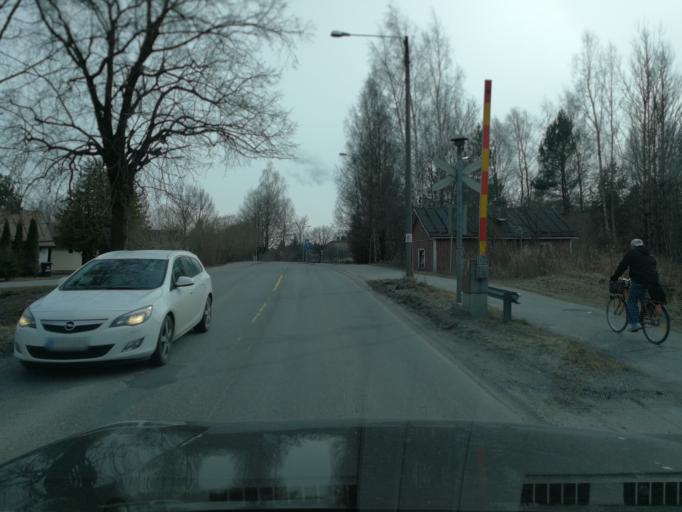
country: FI
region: Uusimaa
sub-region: Helsinki
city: Lohja
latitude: 60.1951
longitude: 24.0020
